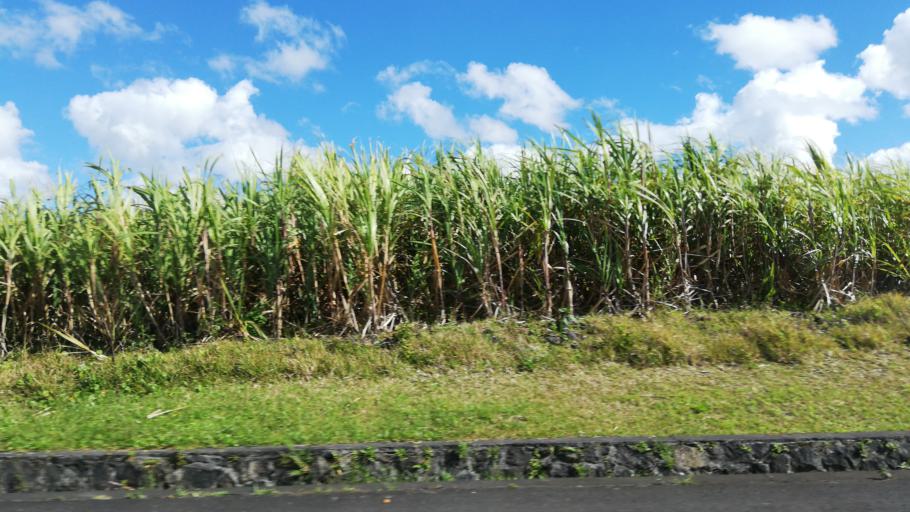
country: MU
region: Moka
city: Quartier Militaire
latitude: -20.2469
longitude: 57.5891
